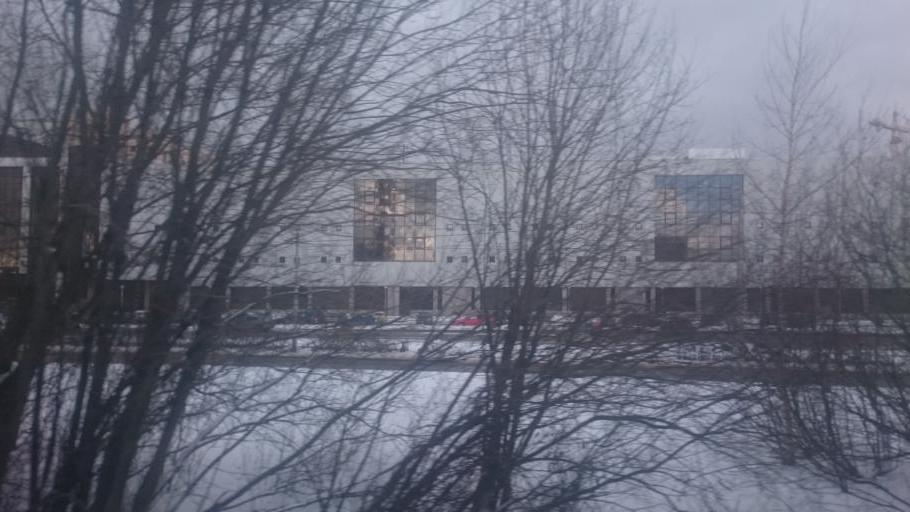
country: RU
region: St.-Petersburg
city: Staraya Derevnya
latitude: 59.9884
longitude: 30.2587
